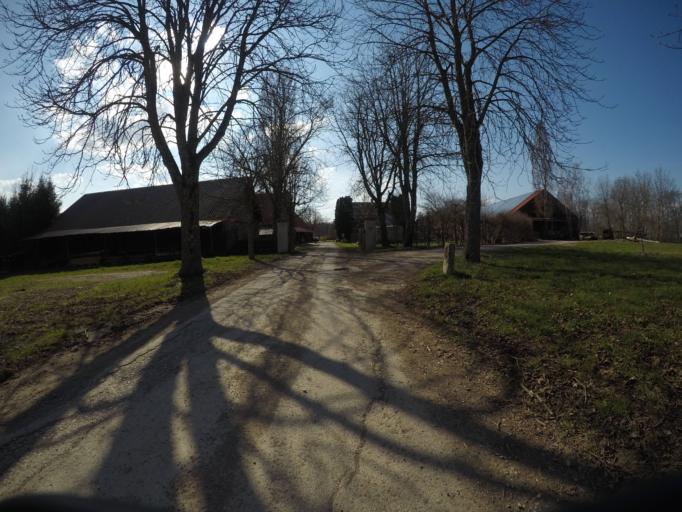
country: DE
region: Baden-Wuerttemberg
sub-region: Tuebingen Region
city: Dusslingen
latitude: 48.4682
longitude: 9.0334
